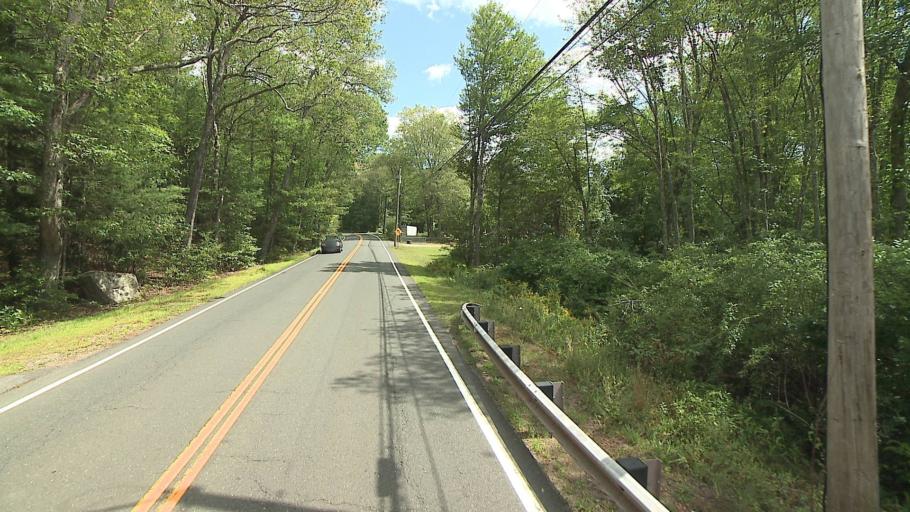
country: US
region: Connecticut
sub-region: Tolland County
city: Crystal Lake
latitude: 41.9325
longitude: -72.3549
